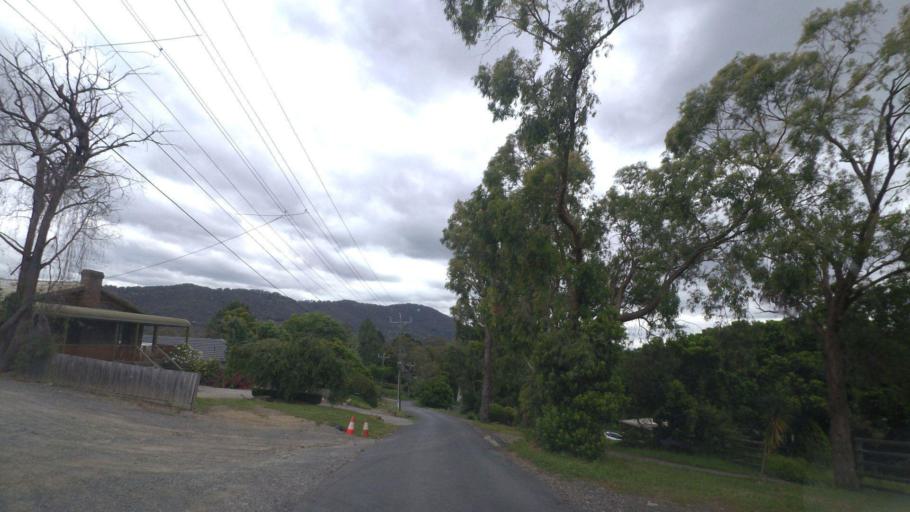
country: AU
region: Victoria
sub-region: Yarra Ranges
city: Mount Evelyn
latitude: -37.7890
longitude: 145.3651
